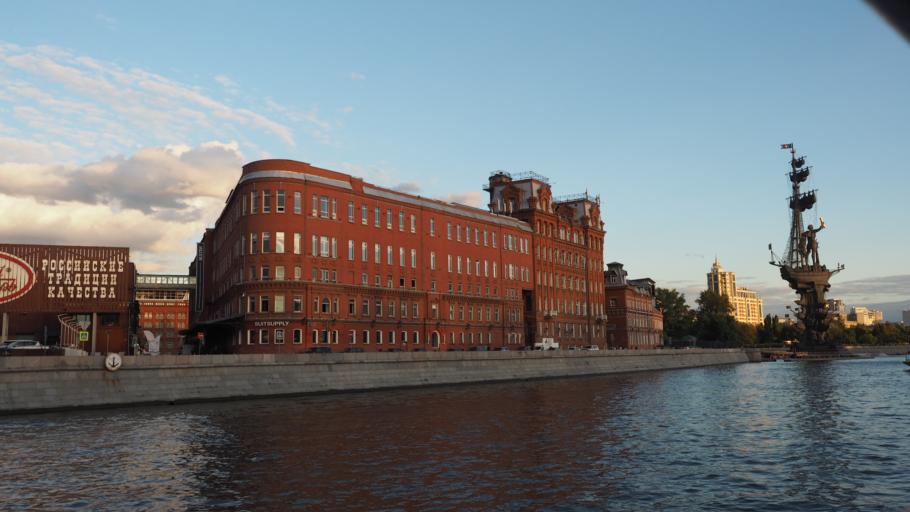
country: RU
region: Moscow
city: Moscow
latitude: 55.7421
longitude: 37.6078
